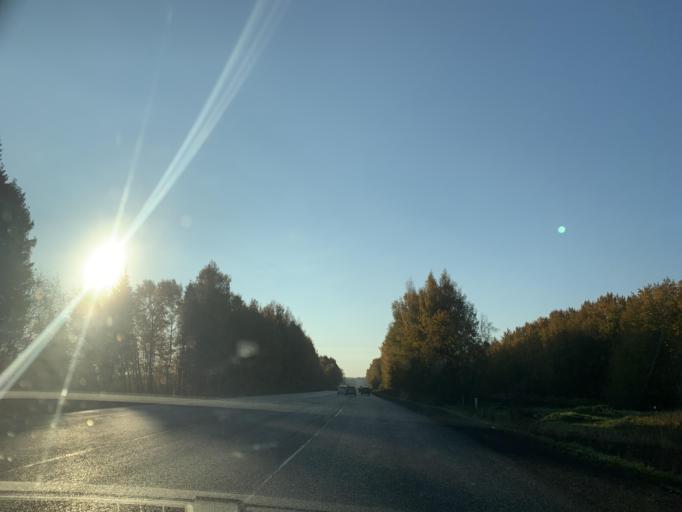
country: RU
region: Jaroslavl
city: Konstantinovskiy
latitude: 57.8051
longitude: 39.5891
